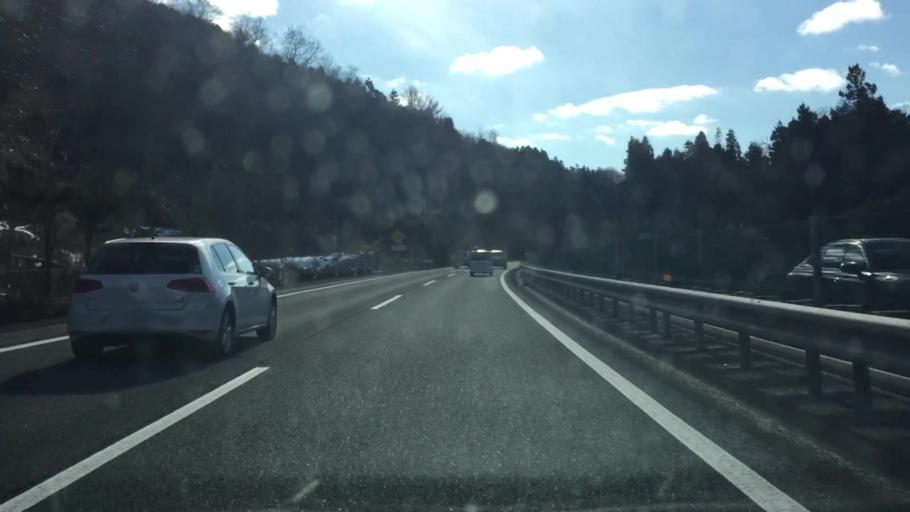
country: JP
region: Gunma
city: Numata
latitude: 36.6398
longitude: 139.0787
